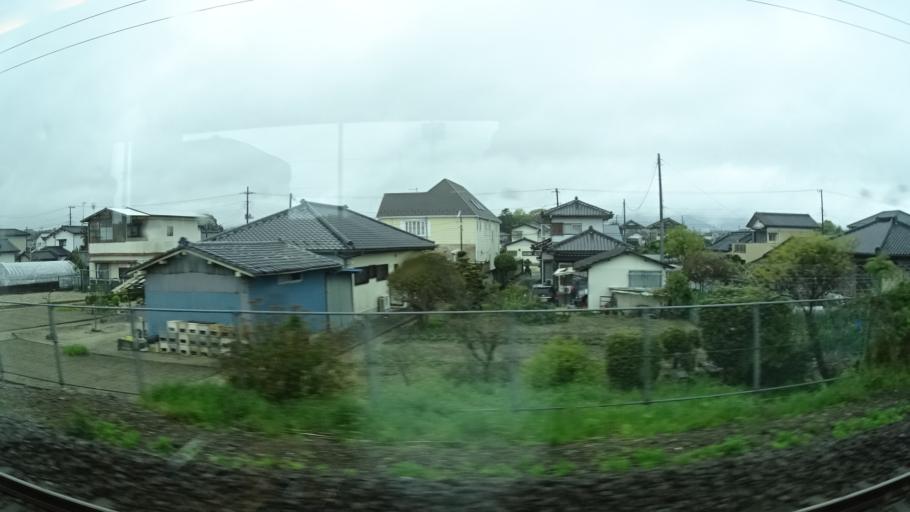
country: JP
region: Ibaraki
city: Kitaibaraki
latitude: 36.7735
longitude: 140.7393
